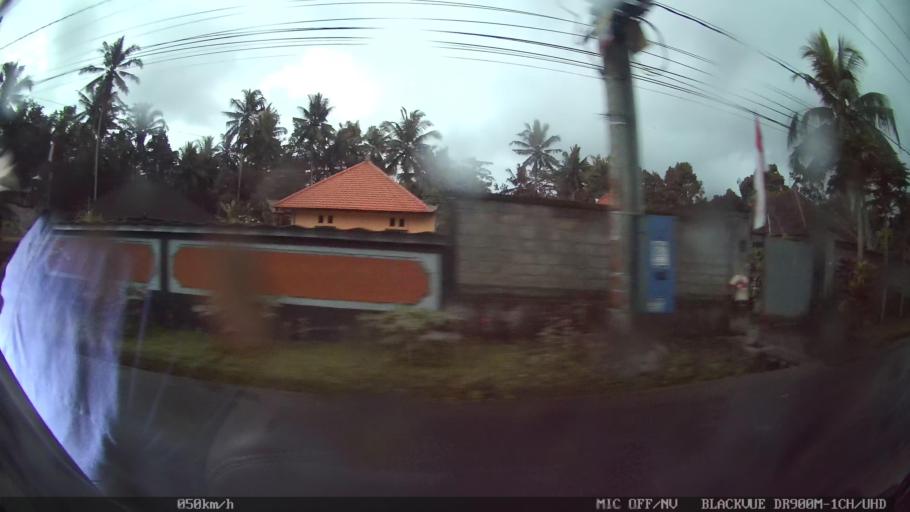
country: ID
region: Bali
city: Banjar Tengah
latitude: -8.5010
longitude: 115.1886
